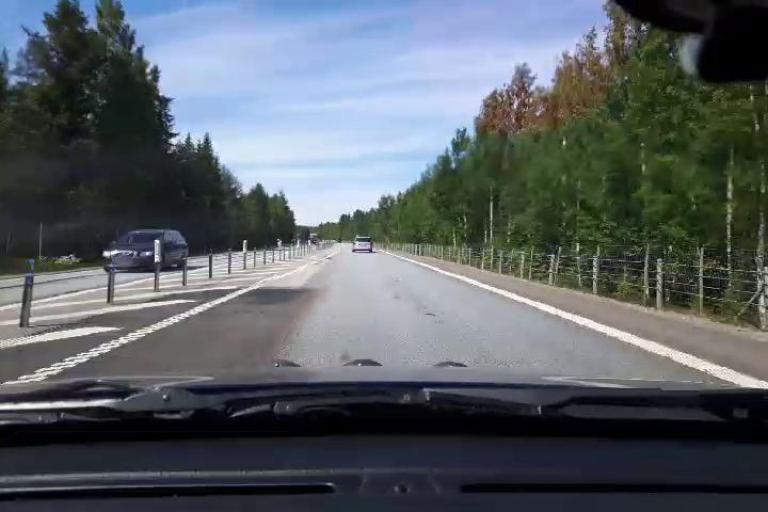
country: SE
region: Gaevleborg
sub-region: Gavle Kommun
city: Norrsundet
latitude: 60.9185
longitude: 17.0134
